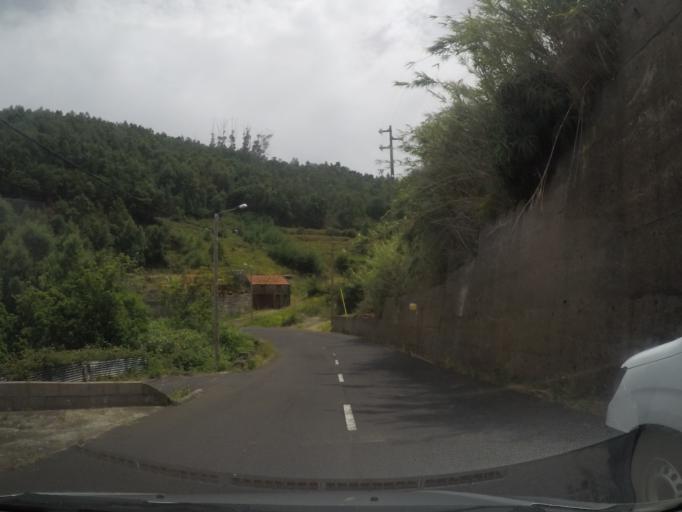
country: PT
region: Madeira
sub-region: Santa Cruz
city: Camacha
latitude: 32.6699
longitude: -16.8395
